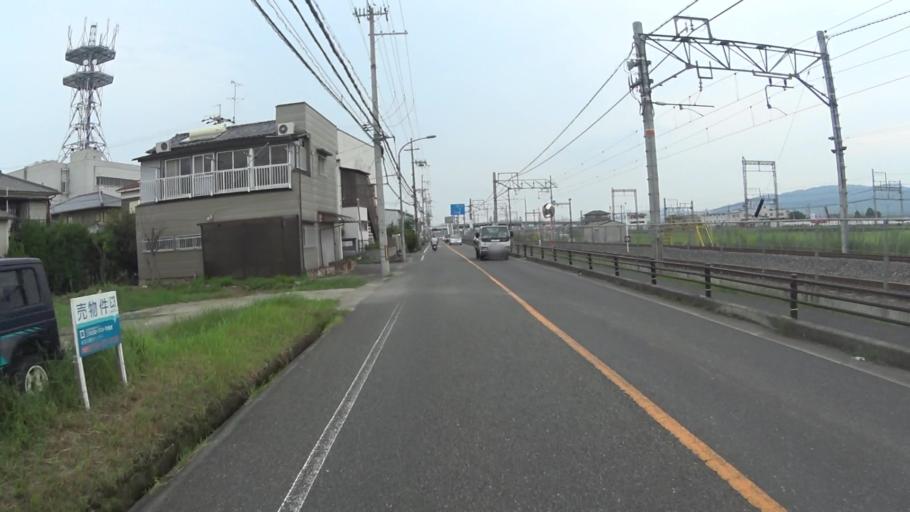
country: JP
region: Nara
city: Nara-shi
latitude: 34.7410
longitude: 135.7945
